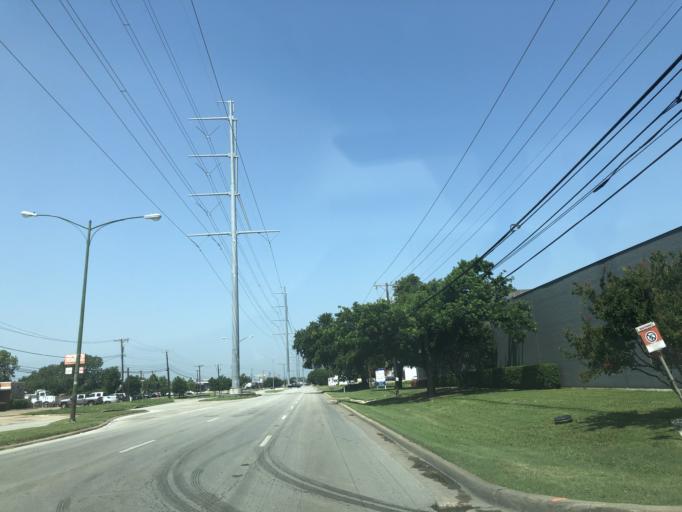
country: US
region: Texas
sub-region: Dallas County
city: Dallas
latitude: 32.8093
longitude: -96.8535
